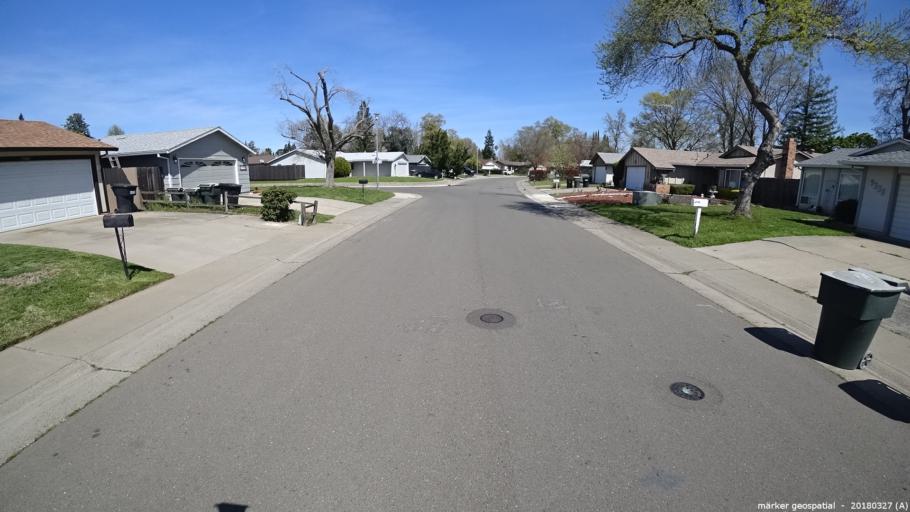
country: US
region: California
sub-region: Sacramento County
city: La Riviera
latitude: 38.5565
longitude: -121.3529
